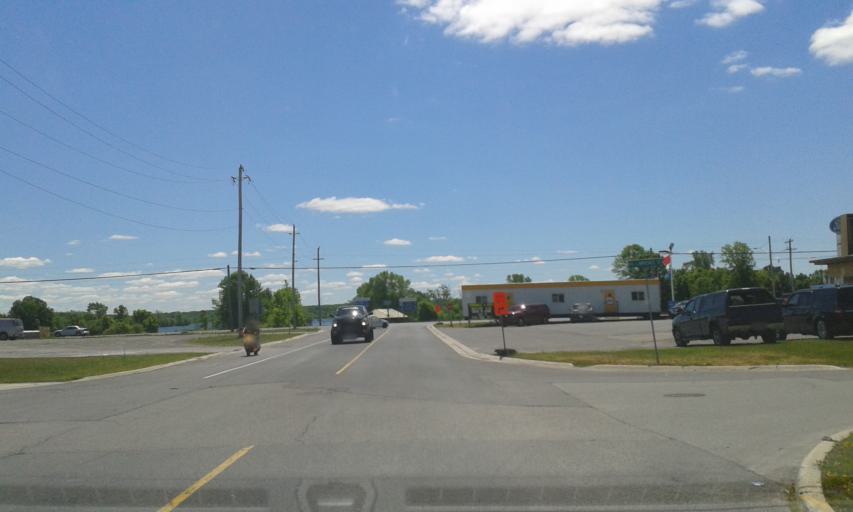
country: US
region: New York
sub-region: St. Lawrence County
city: Massena
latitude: 44.9966
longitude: -74.9873
